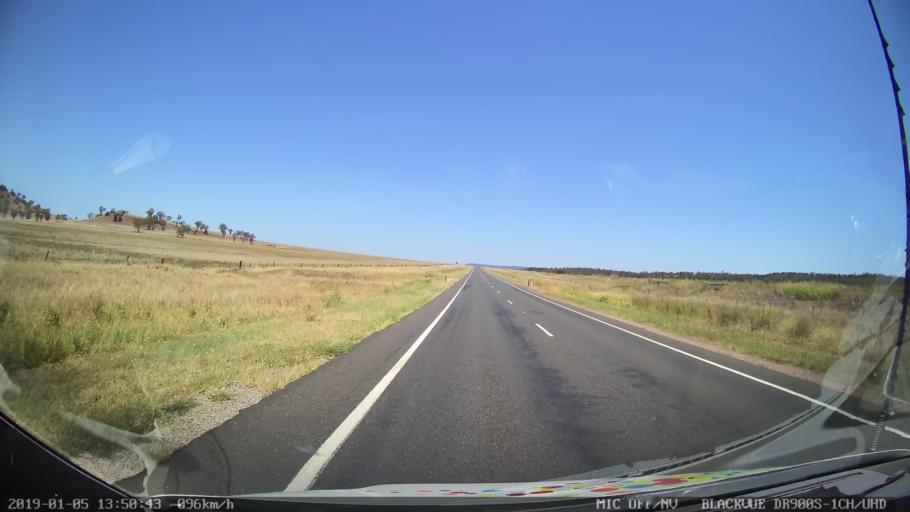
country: AU
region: New South Wales
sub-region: Gunnedah
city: Gunnedah
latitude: -31.0341
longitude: 150.2754
